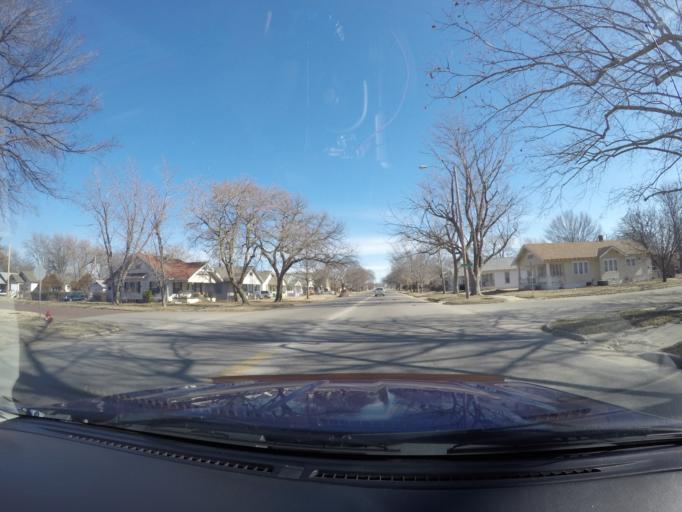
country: US
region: Kansas
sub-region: Sedgwick County
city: Wichita
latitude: 37.6839
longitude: -97.3655
